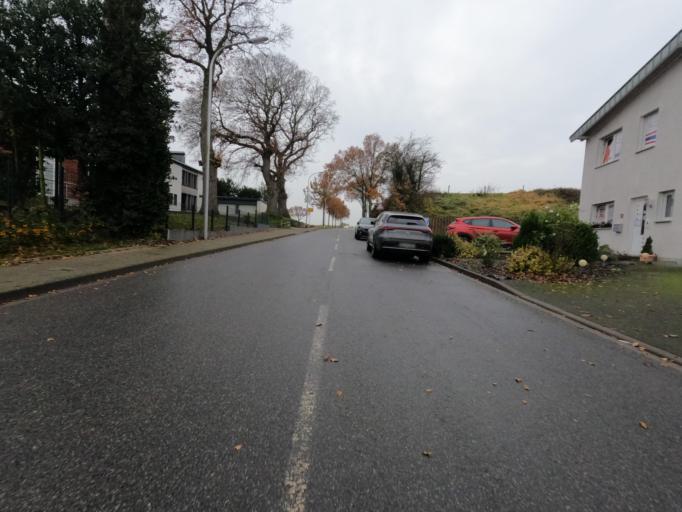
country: DE
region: North Rhine-Westphalia
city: Huckelhoven
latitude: 51.0141
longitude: 6.1721
